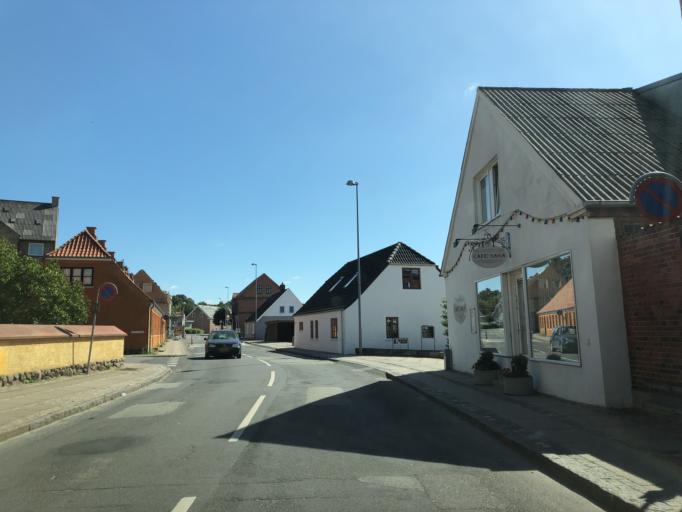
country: DK
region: North Denmark
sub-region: Mariagerfjord Kommune
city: Hobro
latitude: 56.6368
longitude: 9.7929
